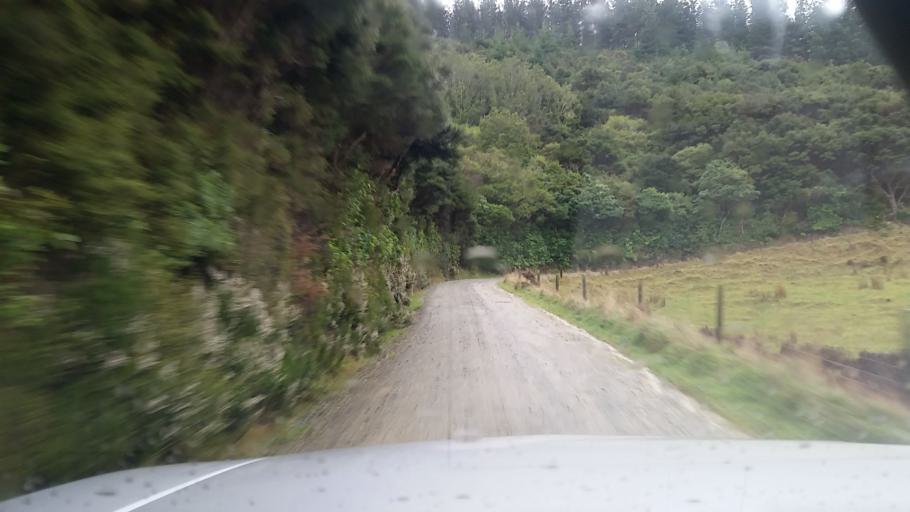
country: NZ
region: Marlborough
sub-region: Marlborough District
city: Picton
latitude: -41.1447
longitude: 174.0508
